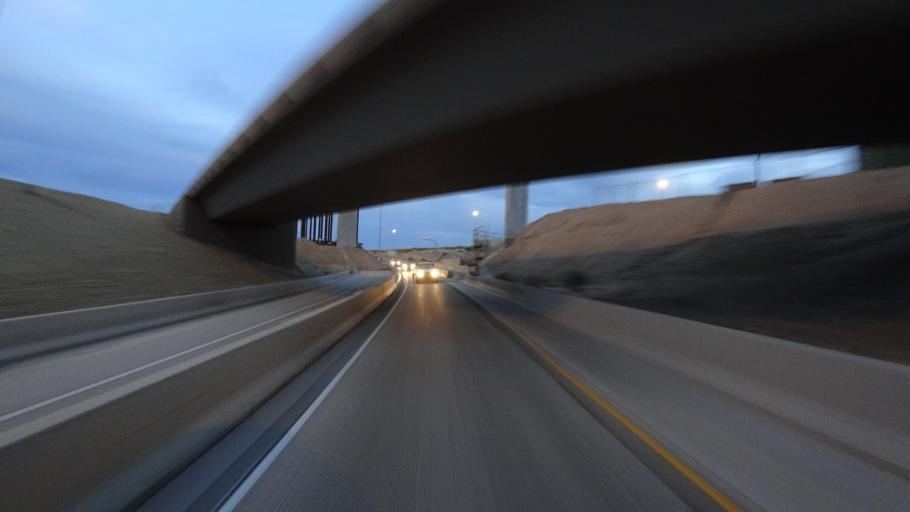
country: US
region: Arizona
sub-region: Maricopa County
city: Goodyear
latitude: 33.4631
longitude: -112.4242
